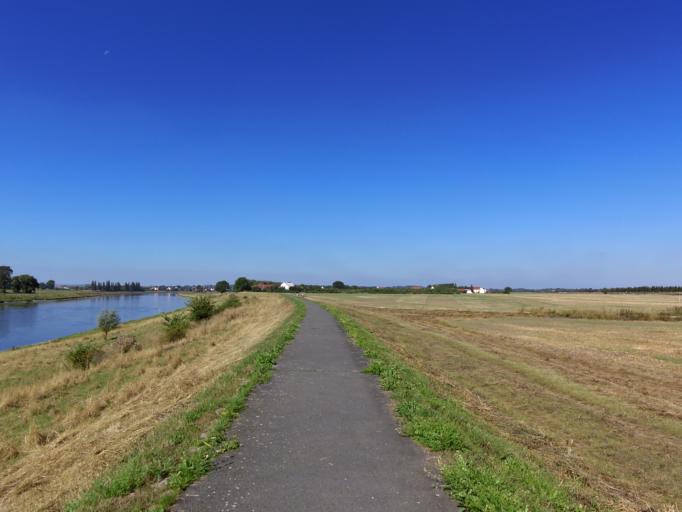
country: DE
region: Saxony
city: Riesa
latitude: 51.3487
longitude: 13.2765
